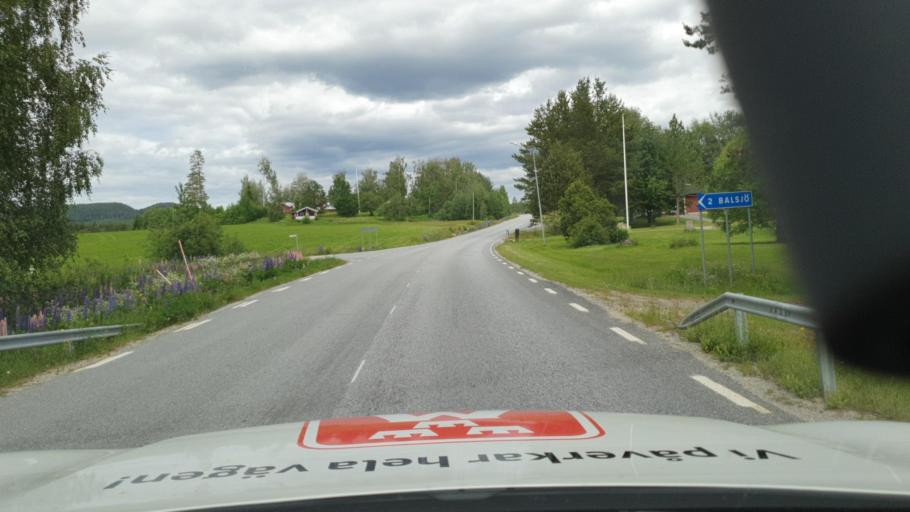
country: SE
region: Vaesterbotten
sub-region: Bjurholms Kommun
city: Bjurholm
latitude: 63.9139
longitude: 19.0896
